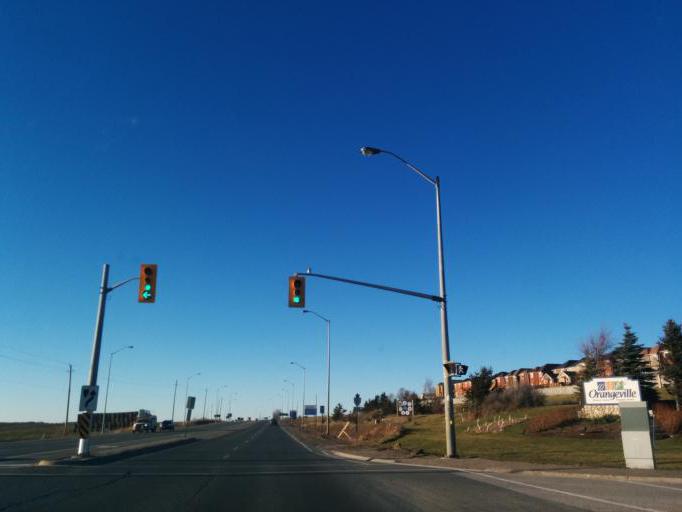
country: CA
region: Ontario
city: Orangeville
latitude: 43.9156
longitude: -80.0713
